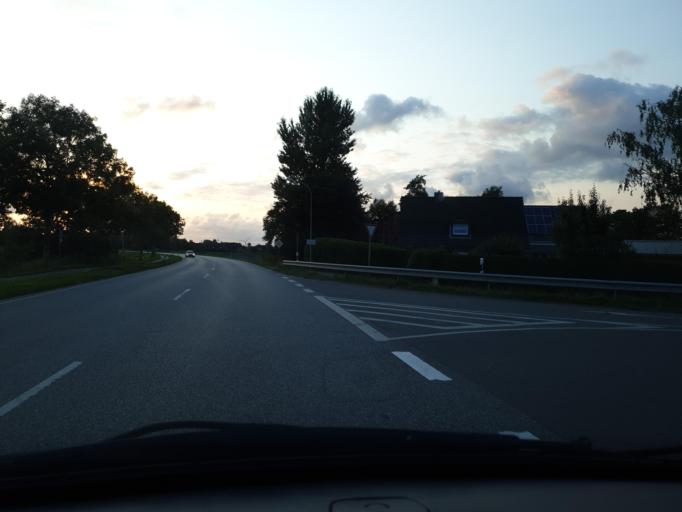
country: DE
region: Schleswig-Holstein
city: Diekhusen-Fahrstedt
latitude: 53.9408
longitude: 9.0240
